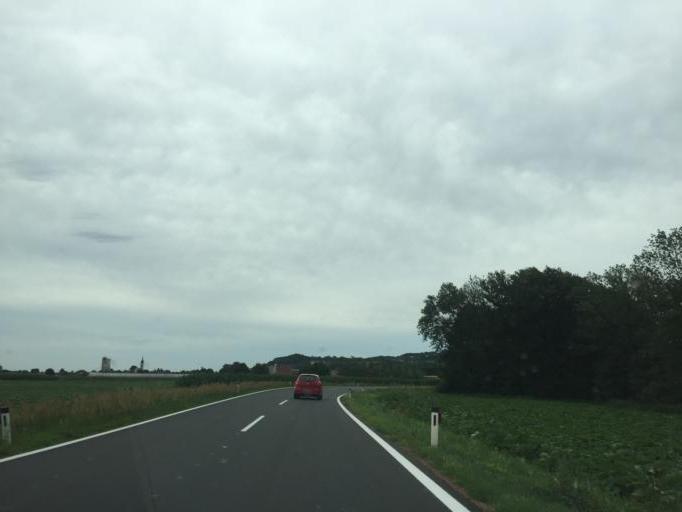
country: AT
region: Styria
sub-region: Politischer Bezirk Suedoststeiermark
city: Mureck
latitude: 46.7076
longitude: 15.7539
